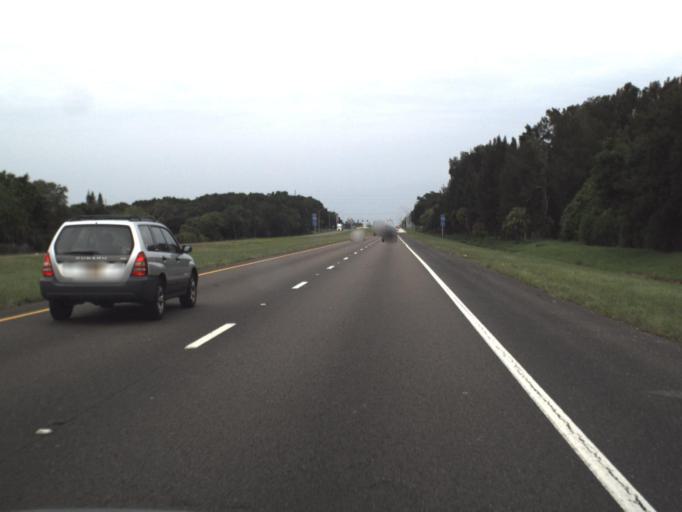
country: US
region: Florida
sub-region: Manatee County
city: Samoset
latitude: 27.4402
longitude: -82.5302
